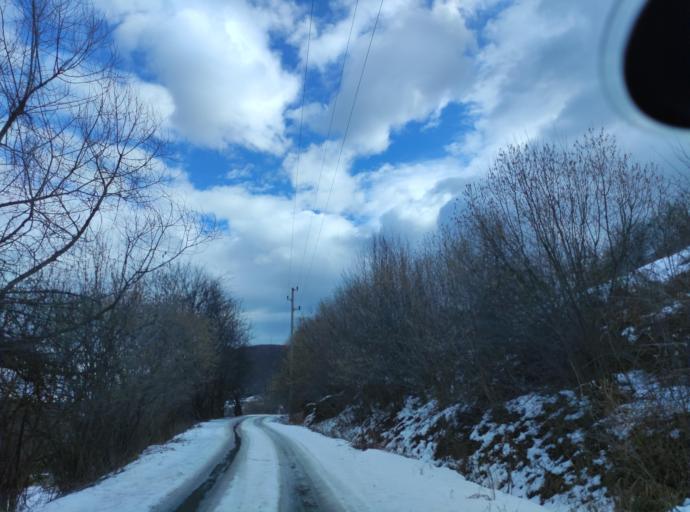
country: BG
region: Montana
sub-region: Obshtina Chiprovtsi
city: Chiprovtsi
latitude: 43.3776
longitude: 22.8687
